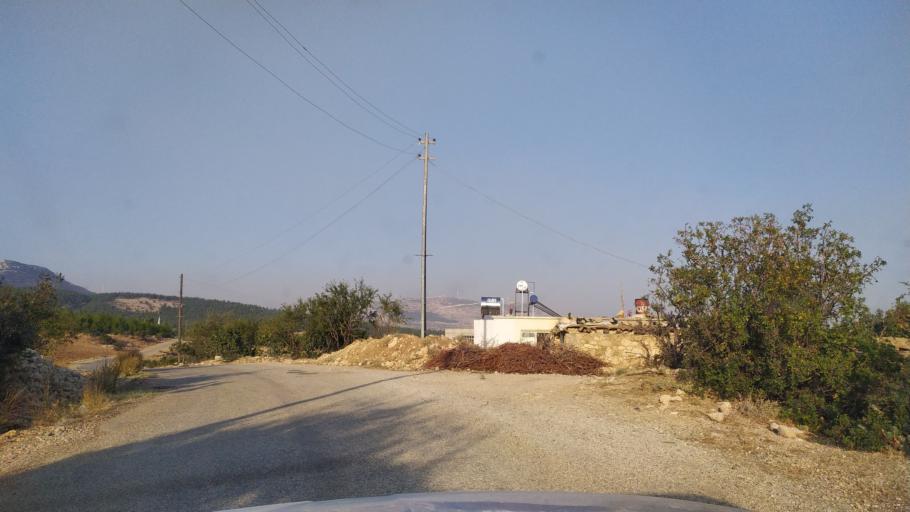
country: TR
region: Mersin
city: Mut
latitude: 36.6831
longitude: 33.1923
